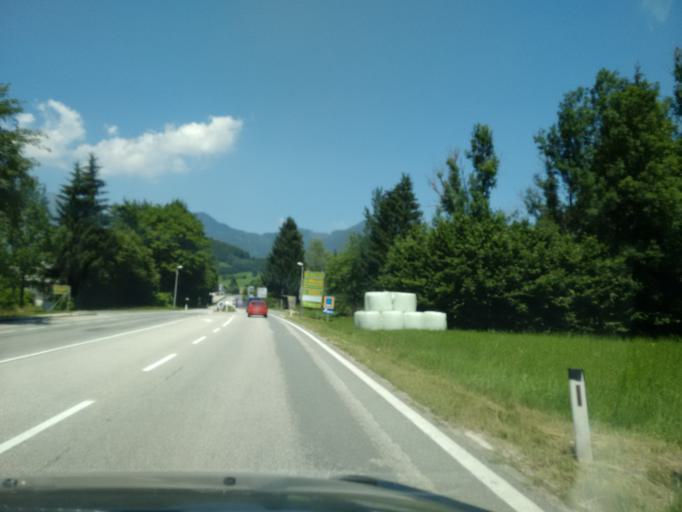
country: AT
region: Upper Austria
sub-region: Politischer Bezirk Gmunden
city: Bad Ischl
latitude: 47.6950
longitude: 13.6236
